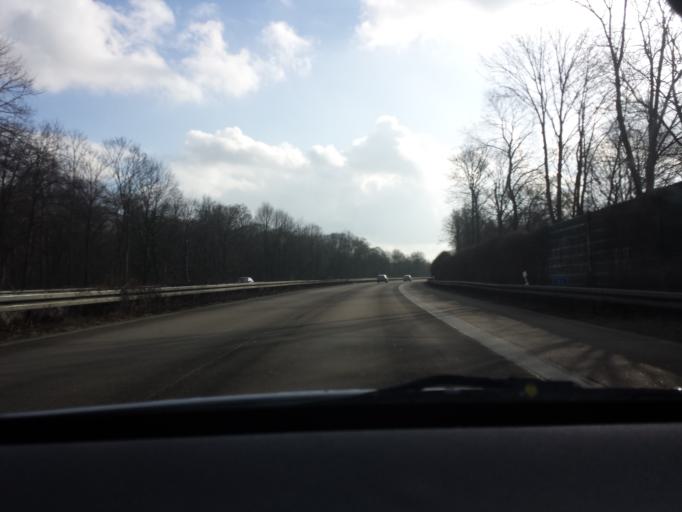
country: DE
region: North Rhine-Westphalia
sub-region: Regierungsbezirk Dusseldorf
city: Hilden
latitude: 51.1650
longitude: 6.8890
